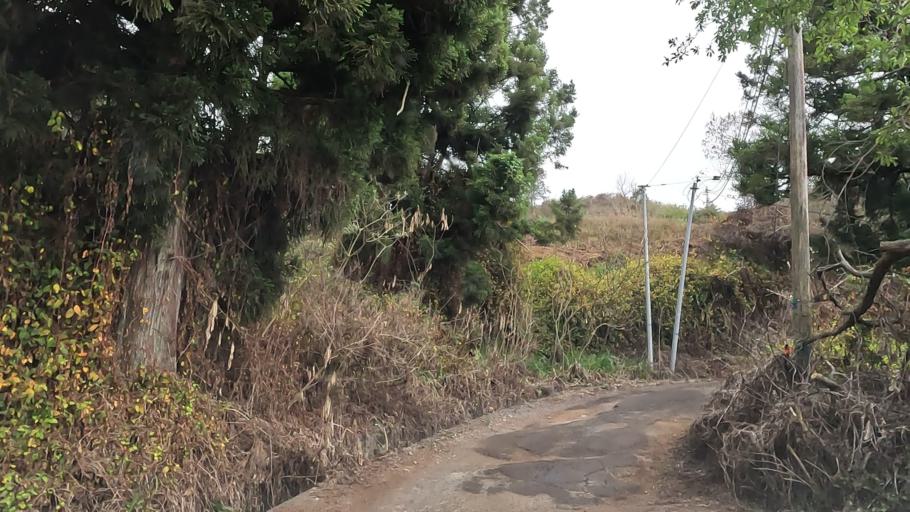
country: RE
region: Reunion
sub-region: Reunion
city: Le Tampon
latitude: -21.2160
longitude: 55.5347
